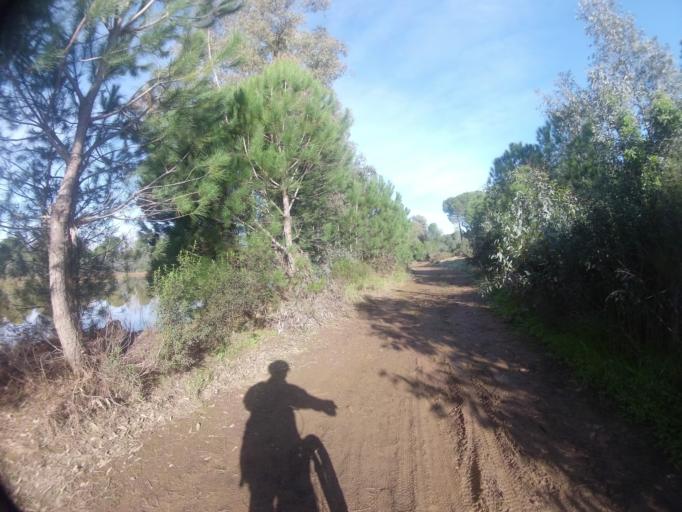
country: ES
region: Andalusia
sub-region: Provincia de Huelva
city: Gibraleon
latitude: 37.3829
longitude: -6.9786
